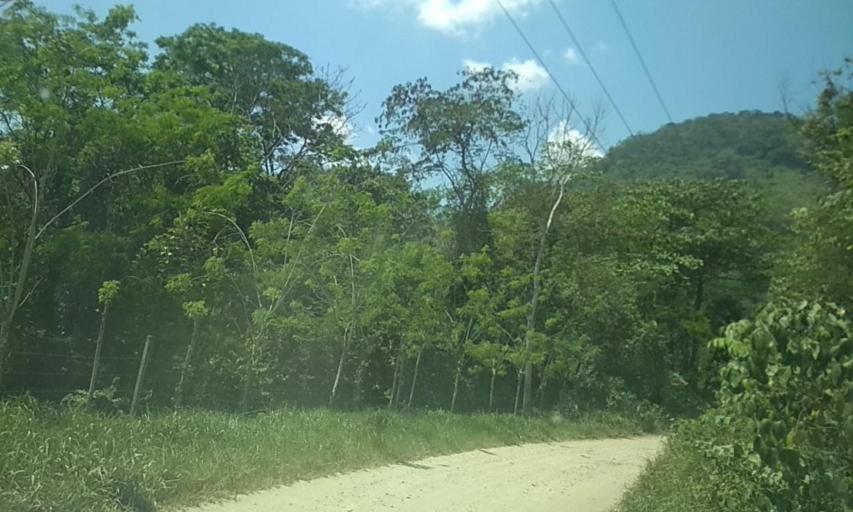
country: MX
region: Chiapas
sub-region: Tecpatan
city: Raudales Malpaso
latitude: 17.2809
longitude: -93.8308
